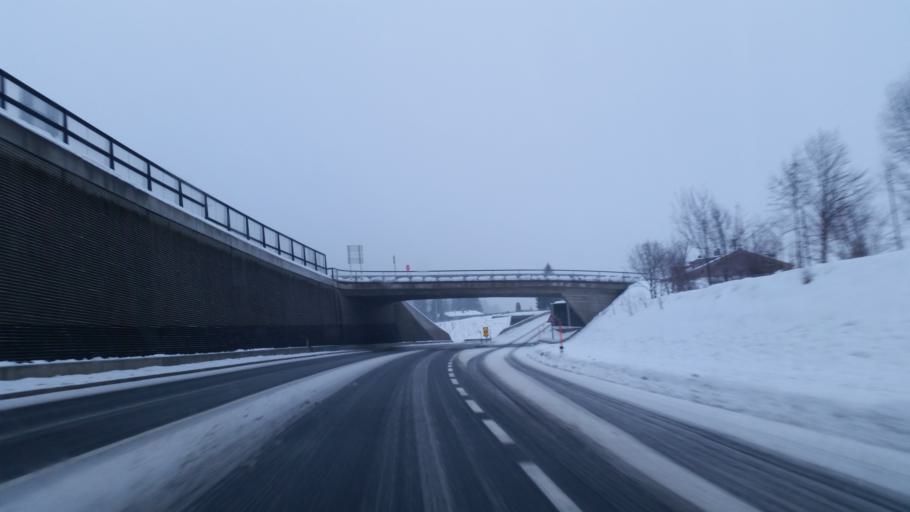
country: AT
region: Tyrol
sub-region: Politischer Bezirk Kufstein
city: Ellmau
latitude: 47.5154
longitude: 12.2999
